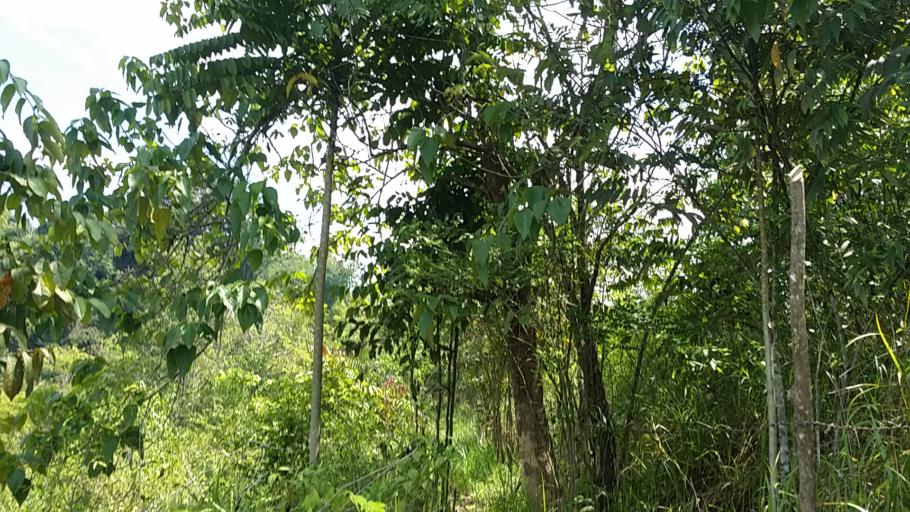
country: PH
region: Davao
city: Lacson
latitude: 7.2118
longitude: 125.4315
